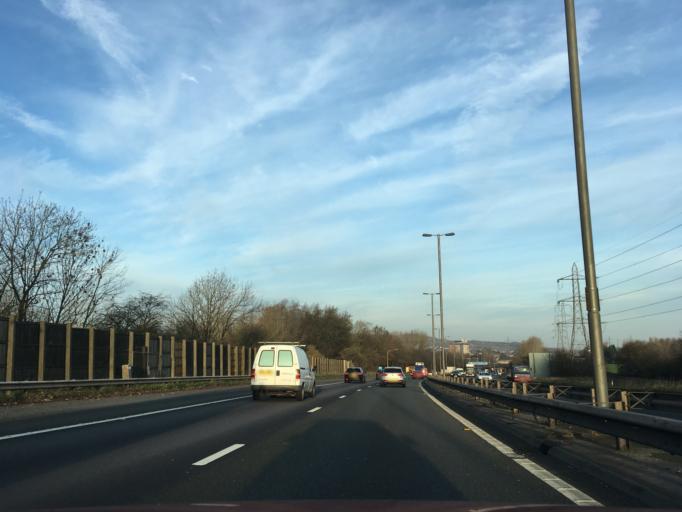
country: GB
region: England
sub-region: Sandwell
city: Oldbury
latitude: 52.4755
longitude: -2.0200
